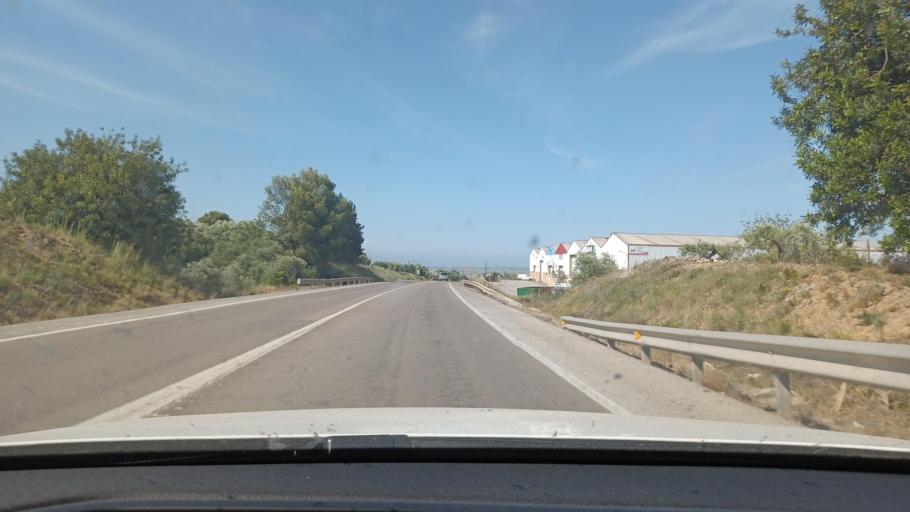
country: ES
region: Catalonia
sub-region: Provincia de Tarragona
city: Sant Carles de la Rapita
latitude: 40.6286
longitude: 0.5806
